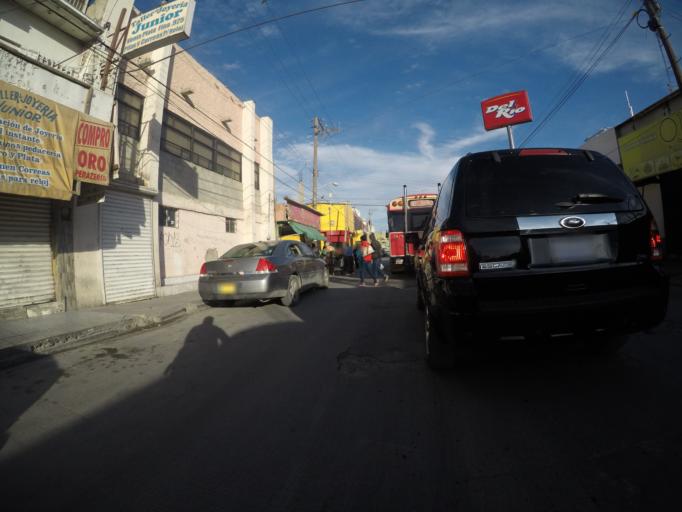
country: MX
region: Chihuahua
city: Ciudad Juarez
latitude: 31.7359
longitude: -106.4849
